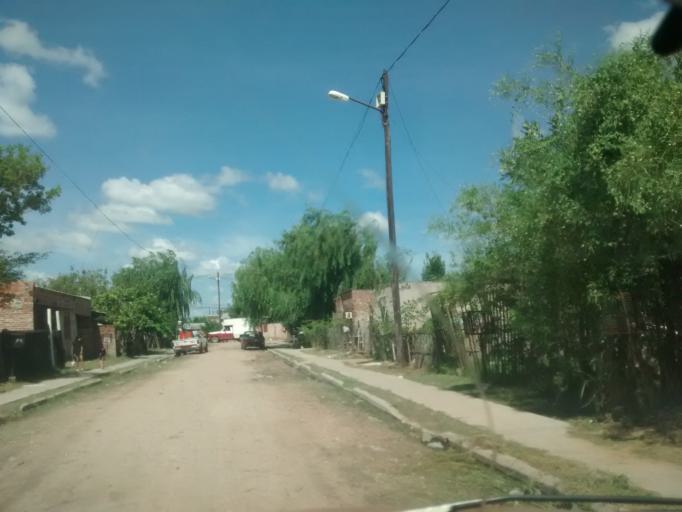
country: AR
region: Chaco
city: Fontana
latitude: -27.4566
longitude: -59.0280
